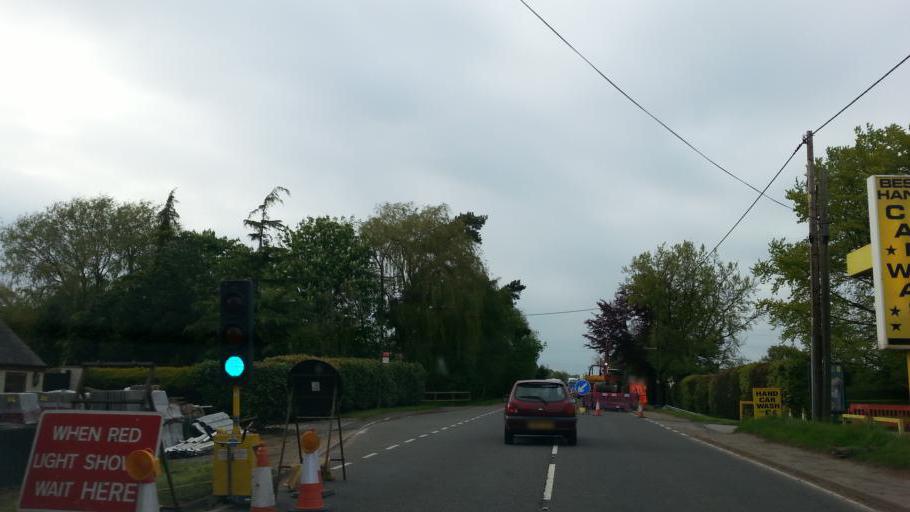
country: GB
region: England
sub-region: Cambridgeshire
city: March
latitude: 52.5693
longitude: 0.0601
